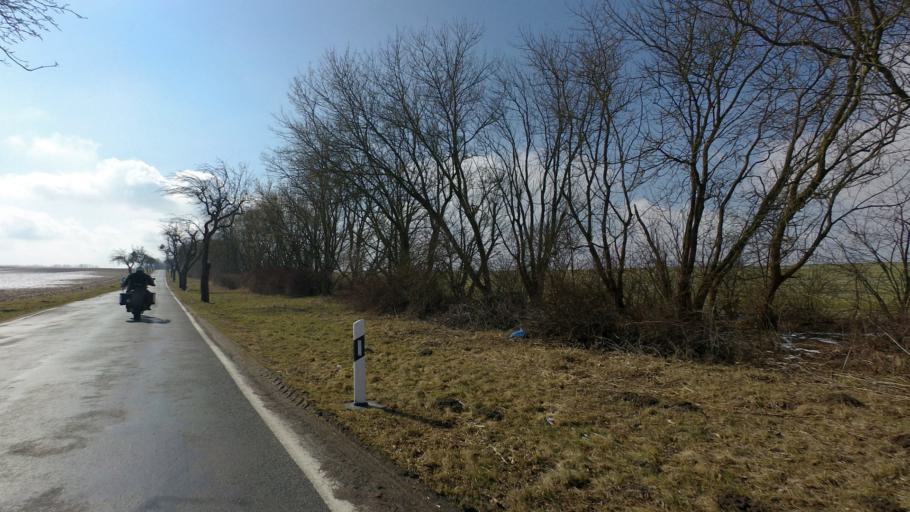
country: DE
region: Brandenburg
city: Melchow
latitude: 52.7047
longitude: 13.7192
